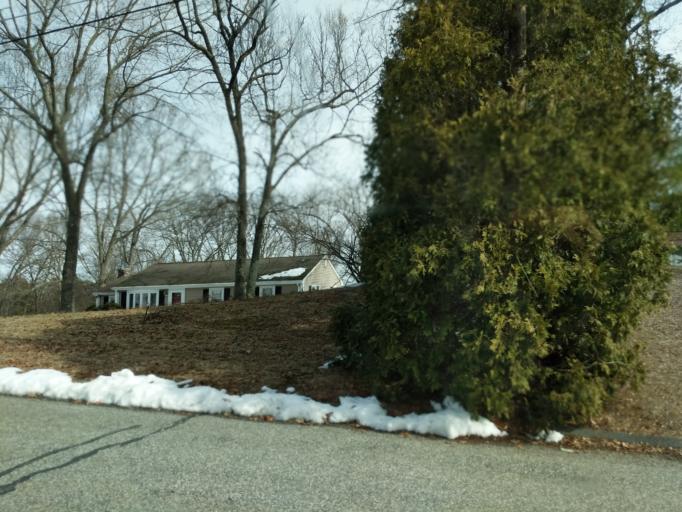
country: US
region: Massachusetts
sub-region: Worcester County
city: Whitinsville
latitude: 42.1070
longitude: -71.6906
